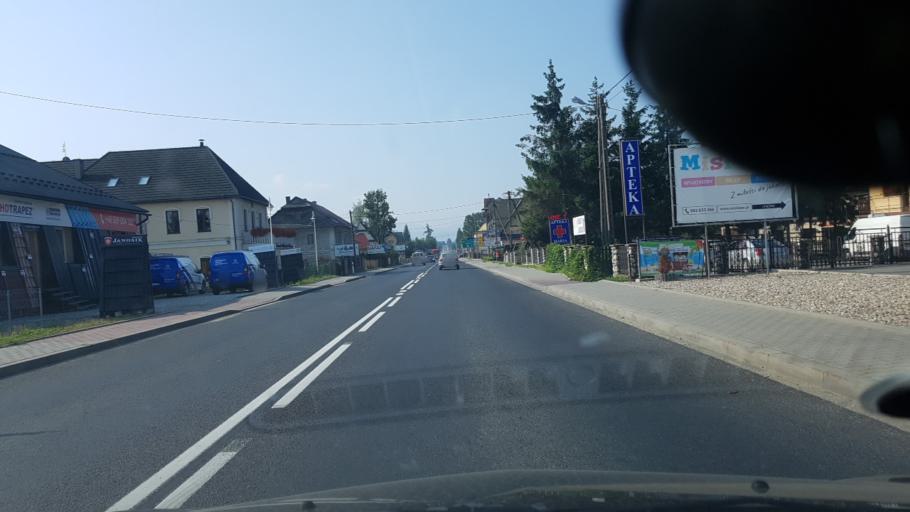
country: PL
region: Lesser Poland Voivodeship
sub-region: Powiat nowotarski
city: Jablonka
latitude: 49.4775
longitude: 19.6935
